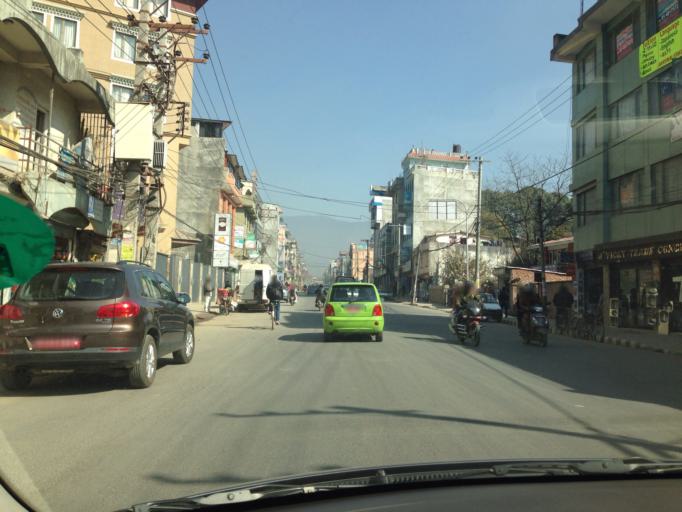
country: NP
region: Central Region
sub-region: Bagmati Zone
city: Kathmandu
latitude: 27.7412
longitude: 85.3382
